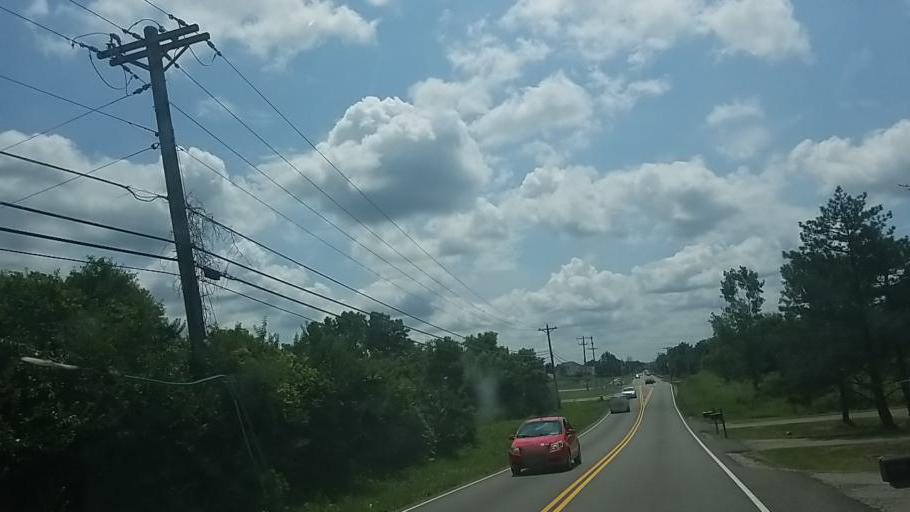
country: US
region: Ohio
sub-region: Fairfield County
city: Pickerington
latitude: 39.9103
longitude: -82.7472
